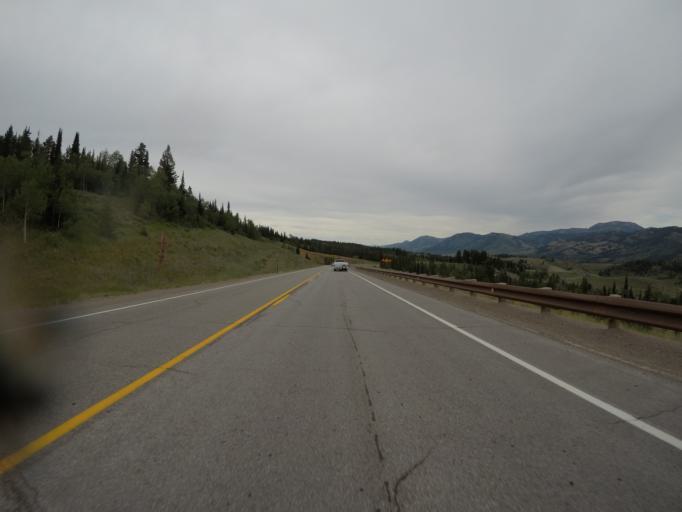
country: US
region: Wyoming
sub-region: Lincoln County
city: Afton
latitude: 42.5100
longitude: -110.9093
